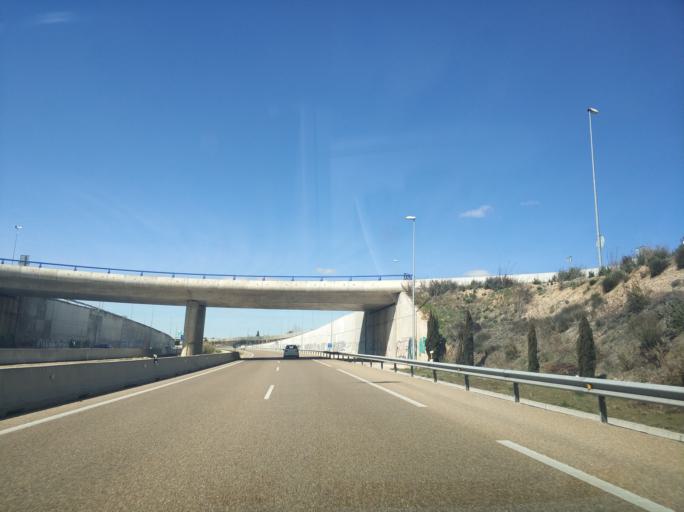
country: ES
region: Castille and Leon
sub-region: Provincia de Valladolid
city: Laguna de Duero
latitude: 41.6078
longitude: -4.7530
